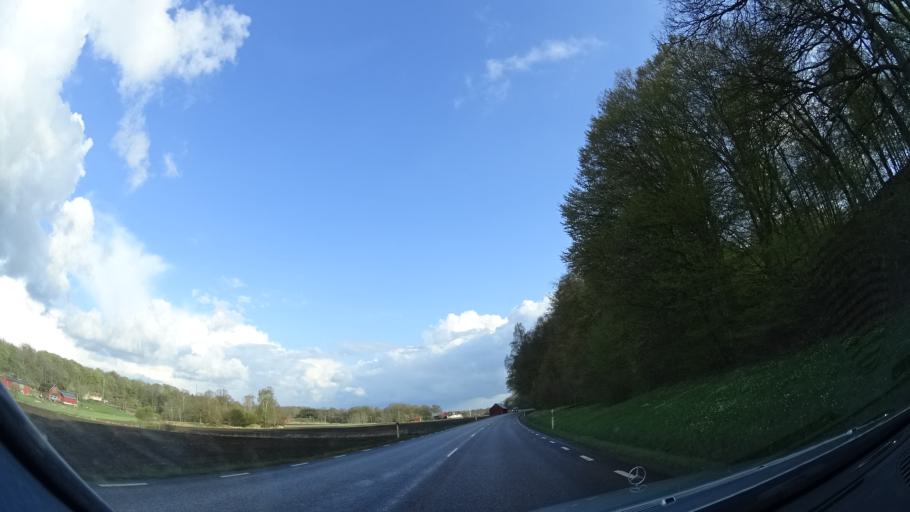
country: SE
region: Skane
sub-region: Klippans Kommun
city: Ljungbyhed
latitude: 56.0339
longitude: 13.2609
